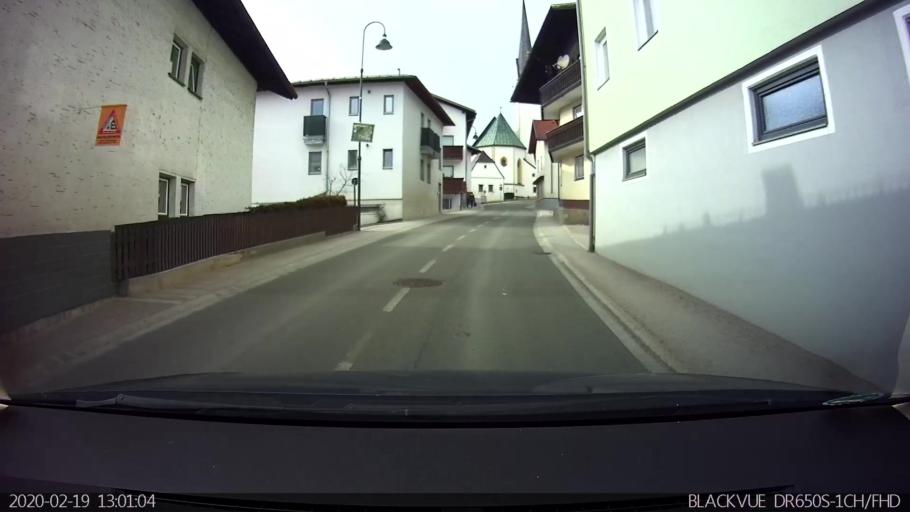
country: AT
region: Tyrol
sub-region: Politischer Bezirk Innsbruck Land
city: Rum
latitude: 47.2868
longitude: 11.4615
